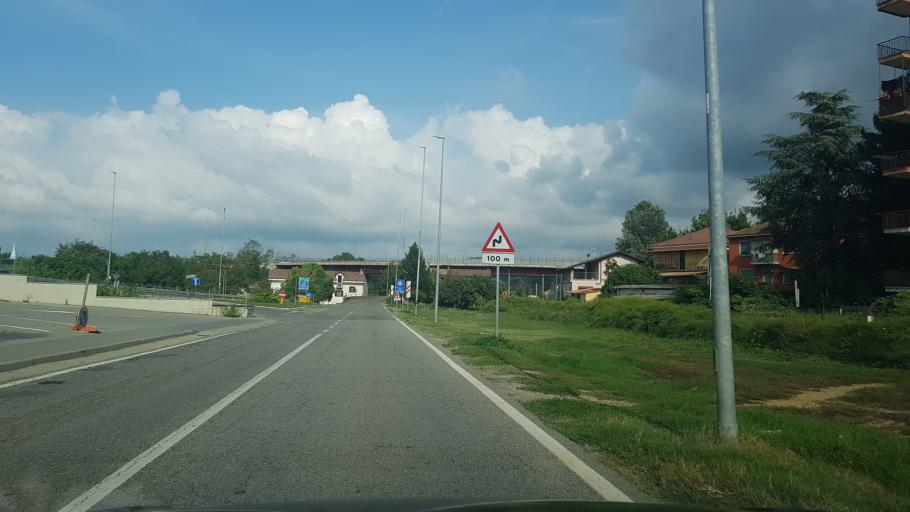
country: IT
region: Piedmont
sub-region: Provincia di Asti
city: Canelli
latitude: 44.7178
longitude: 8.2962
